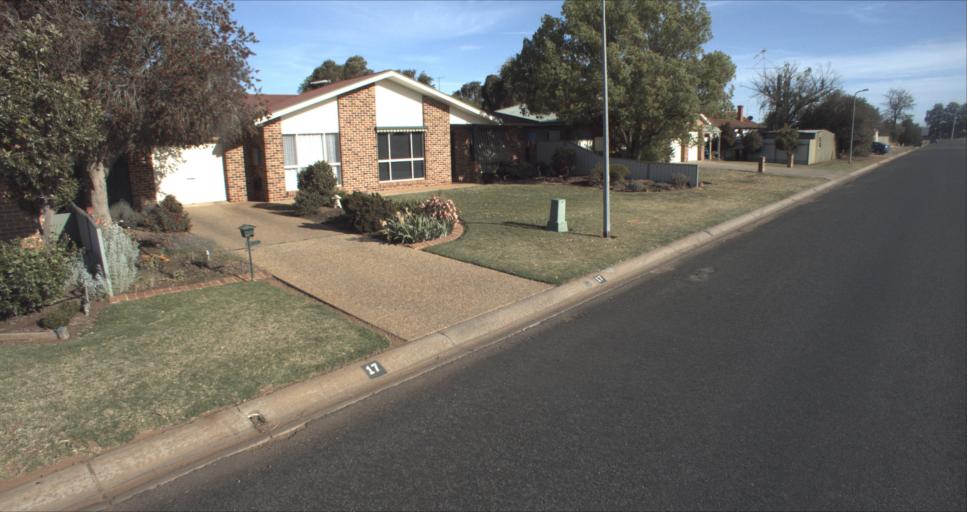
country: AU
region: New South Wales
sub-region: Leeton
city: Leeton
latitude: -34.5438
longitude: 146.3995
